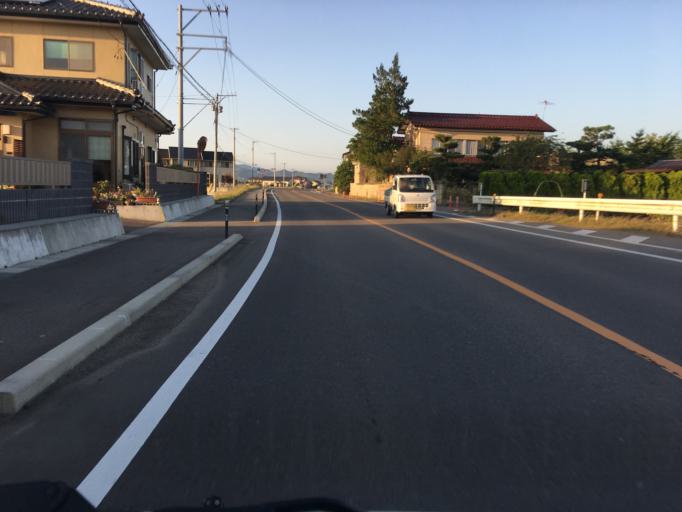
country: JP
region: Fukushima
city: Yanagawamachi-saiwaicho
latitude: 37.8277
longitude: 140.5927
